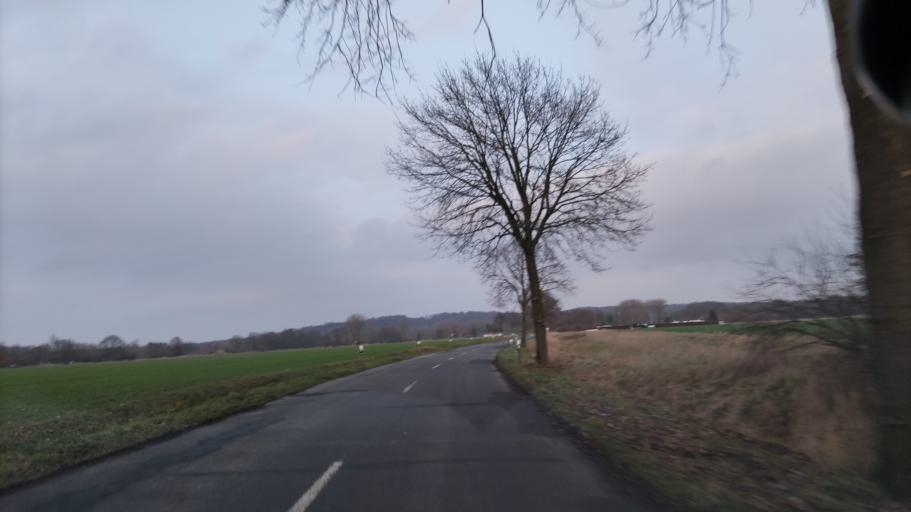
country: DE
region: Mecklenburg-Vorpommern
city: Nostorf
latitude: 53.3564
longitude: 10.6476
